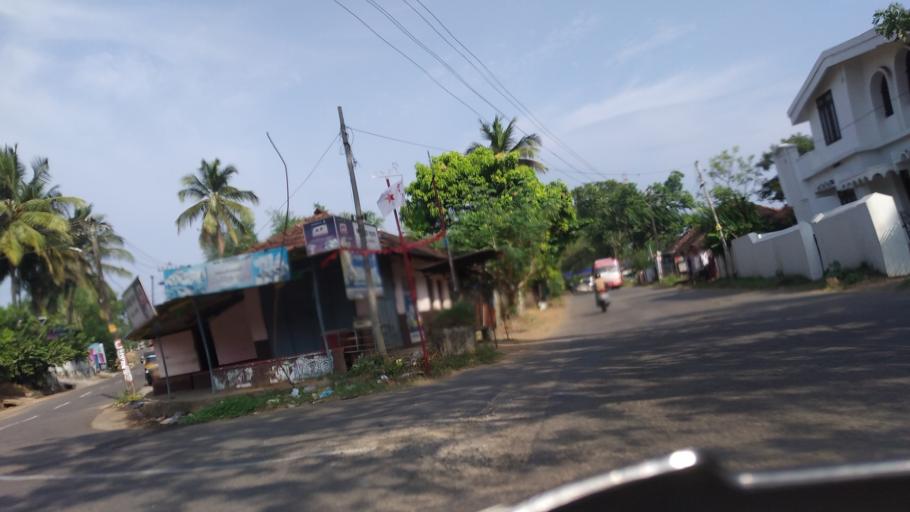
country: IN
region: Kerala
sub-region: Palakkad district
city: Palakkad
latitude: 10.6026
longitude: 76.5412
